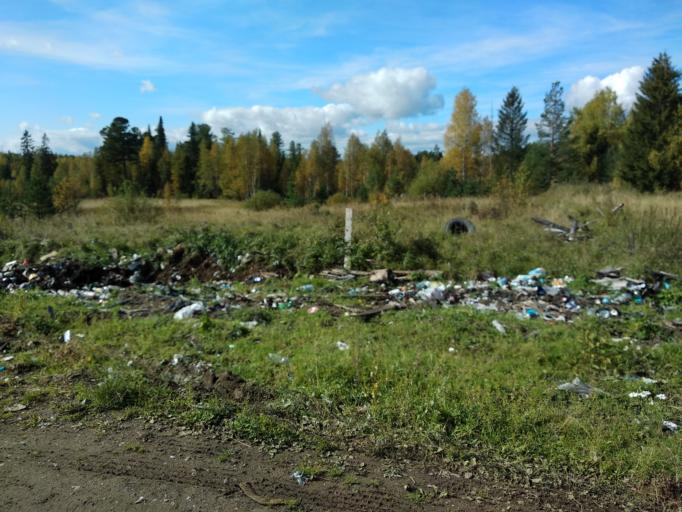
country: RU
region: Sverdlovsk
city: Karpinsk
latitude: 59.9424
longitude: 59.8069
